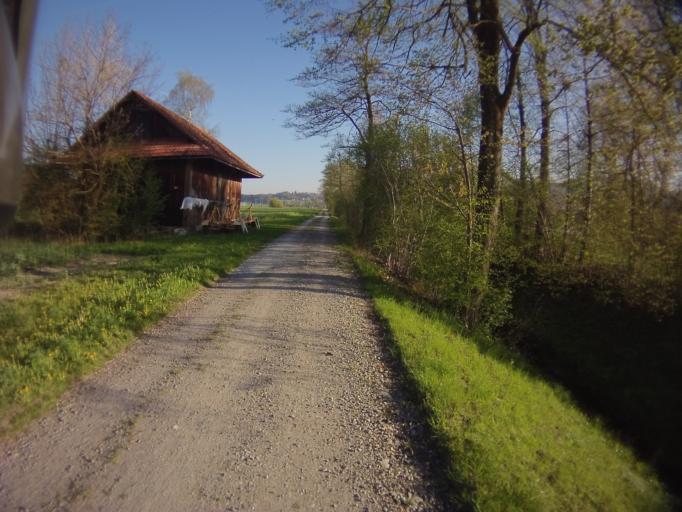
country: CH
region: Zurich
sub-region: Bezirk Affoltern
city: Schachen
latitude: 47.3292
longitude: 8.4658
